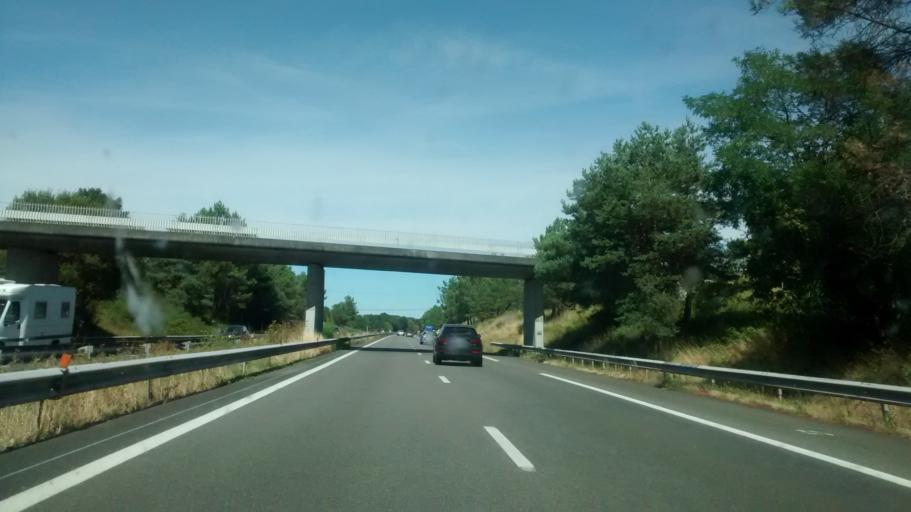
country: FR
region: Poitou-Charentes
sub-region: Departement de la Charente-Maritime
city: Saint-Genis-de-Saintonge
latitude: 45.4535
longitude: -0.6146
